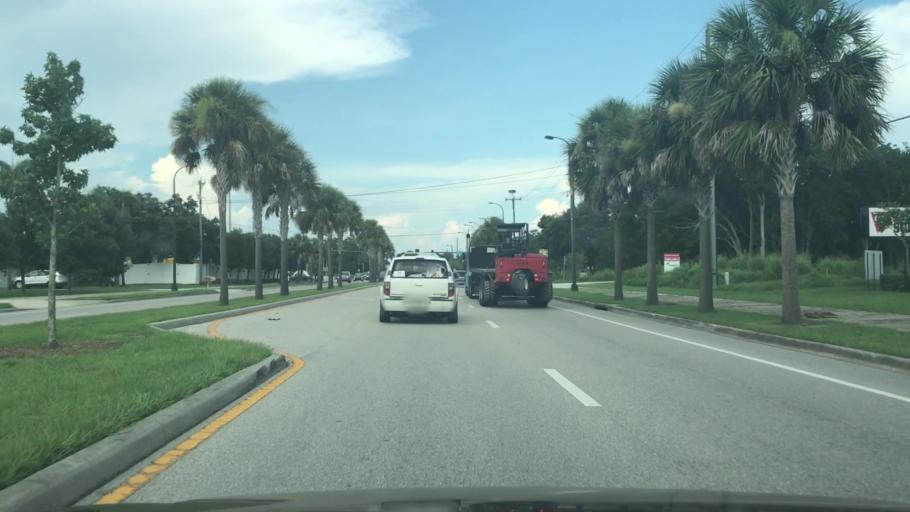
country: US
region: Florida
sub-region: Sarasota County
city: Fruitville
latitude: 27.3384
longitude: -82.4288
